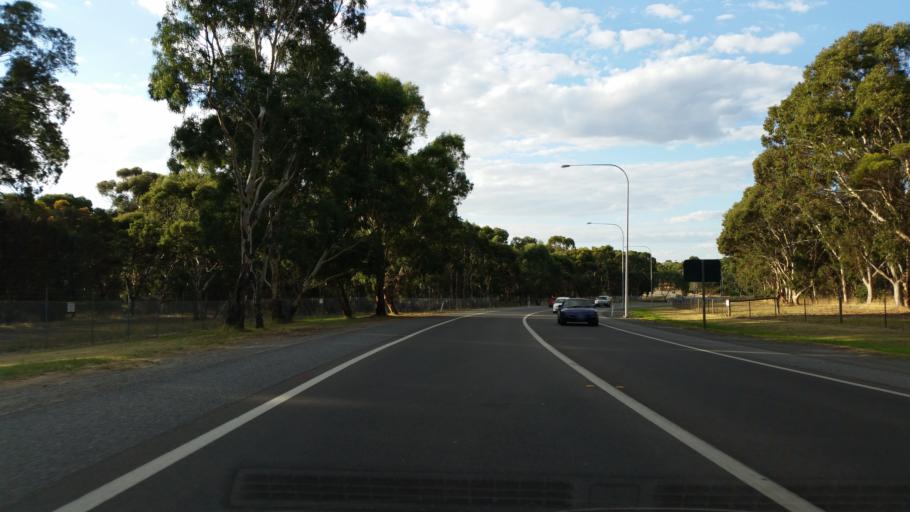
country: AU
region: South Australia
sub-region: Marion
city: Trott Park
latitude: -35.0792
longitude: 138.5818
